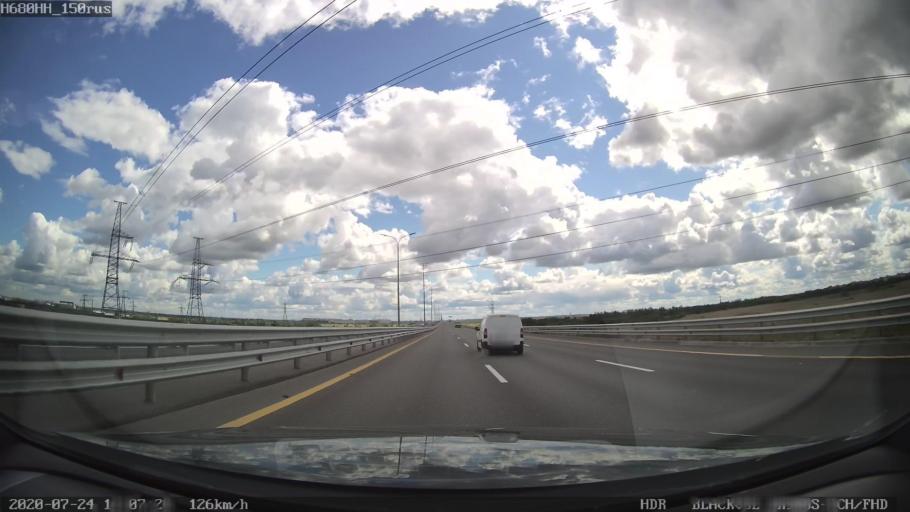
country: RU
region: St.-Petersburg
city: Pushkin
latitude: 59.7564
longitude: 30.4015
